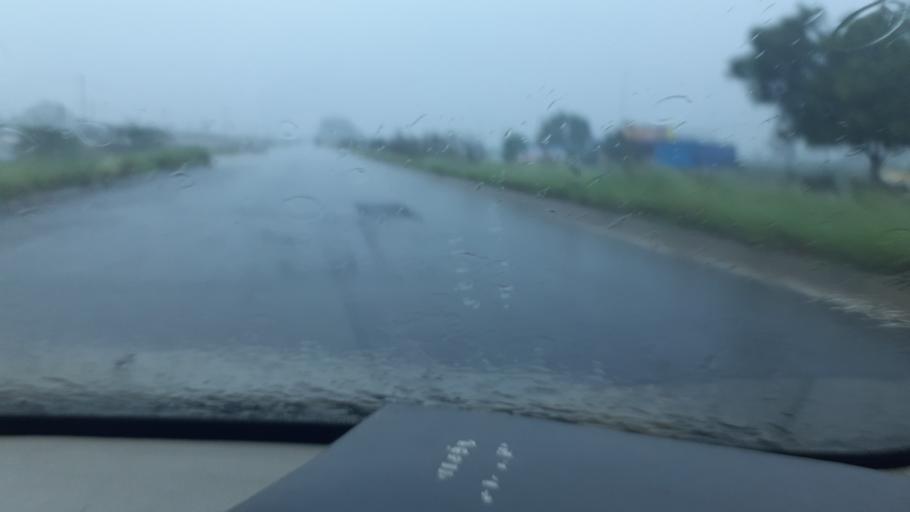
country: IN
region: Tamil Nadu
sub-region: Virudhunagar
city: Sattur
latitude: 9.4421
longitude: 77.9252
